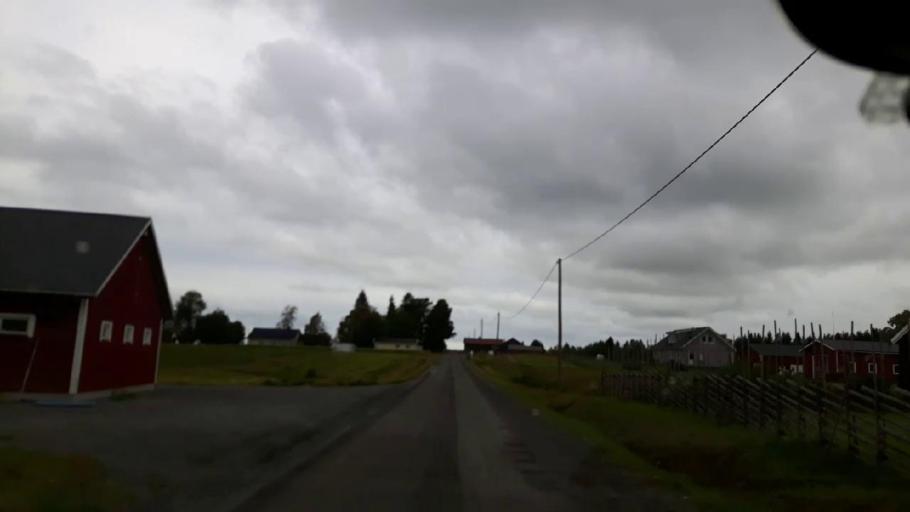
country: SE
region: Jaemtland
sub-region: OEstersunds Kommun
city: Ostersund
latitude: 63.0528
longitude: 14.5658
